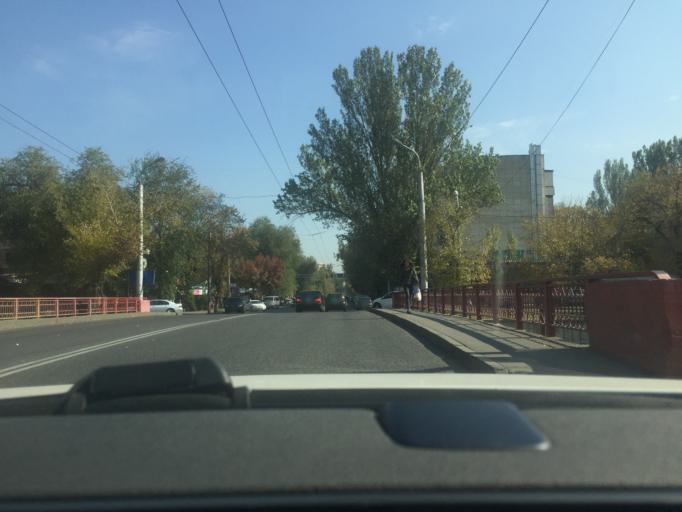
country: KZ
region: Almaty Qalasy
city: Almaty
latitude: 43.2579
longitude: 76.9157
